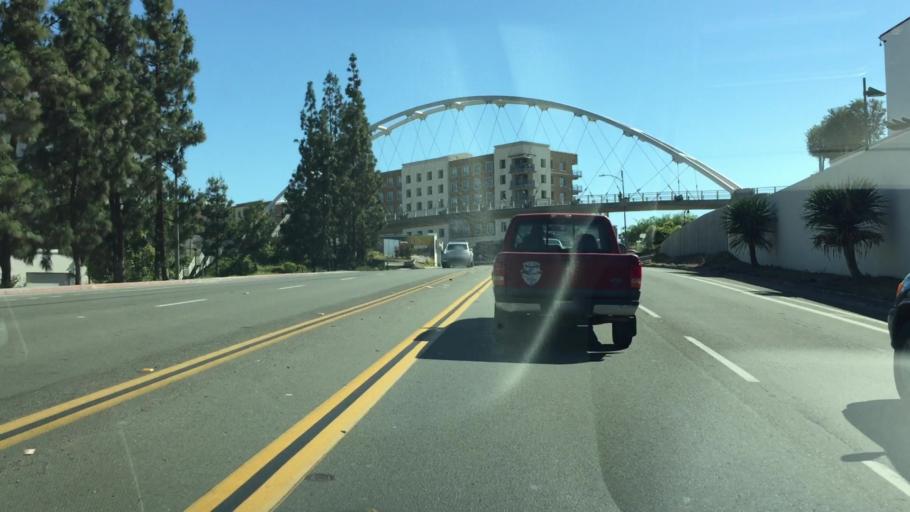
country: US
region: California
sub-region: San Diego County
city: La Mesa
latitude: 32.7736
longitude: -117.0686
